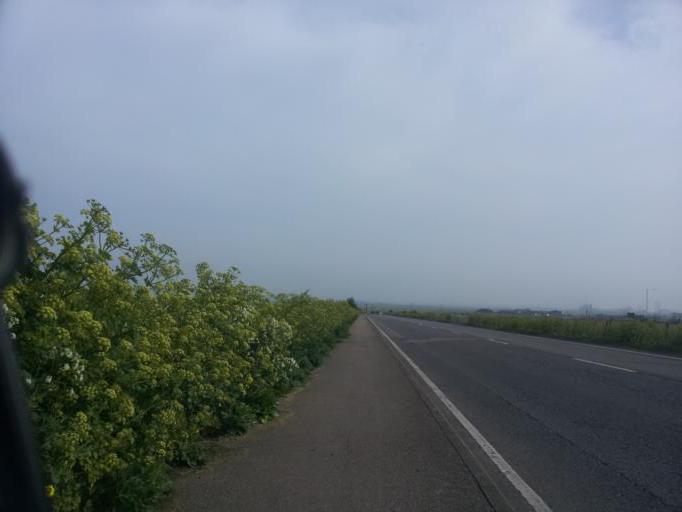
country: GB
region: England
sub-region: Kent
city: Queenborough
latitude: 51.4082
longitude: 0.7716
